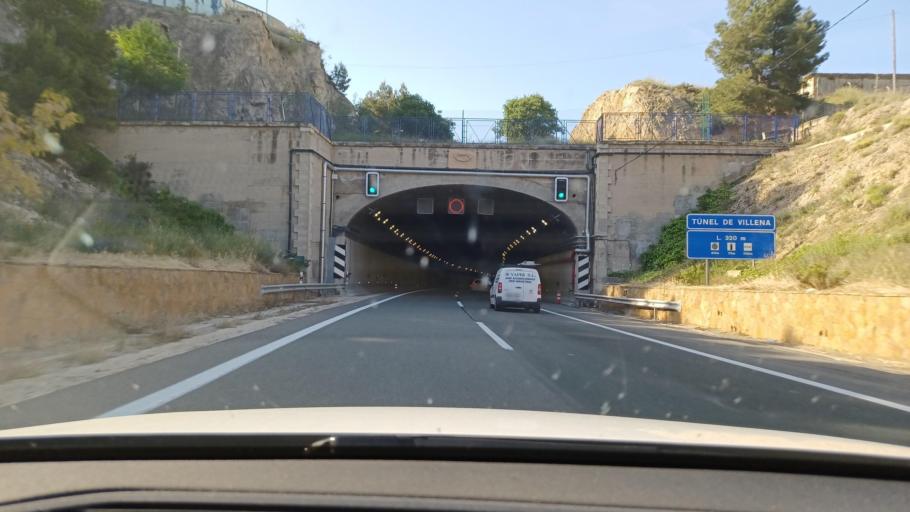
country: ES
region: Valencia
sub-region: Provincia de Alicante
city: Villena
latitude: 38.6362
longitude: -0.8586
